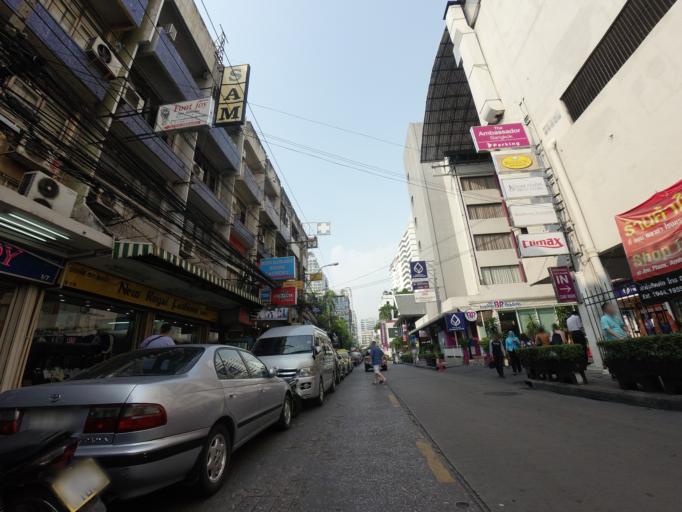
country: TH
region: Bangkok
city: Din Daeng
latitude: 13.7413
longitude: 100.5564
